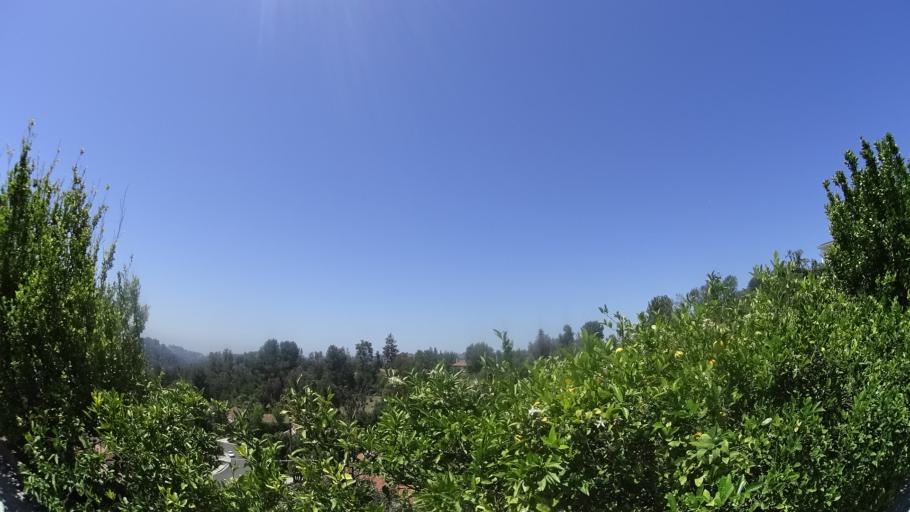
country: US
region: California
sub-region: Los Angeles County
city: Sherman Oaks
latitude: 34.1299
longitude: -118.4465
